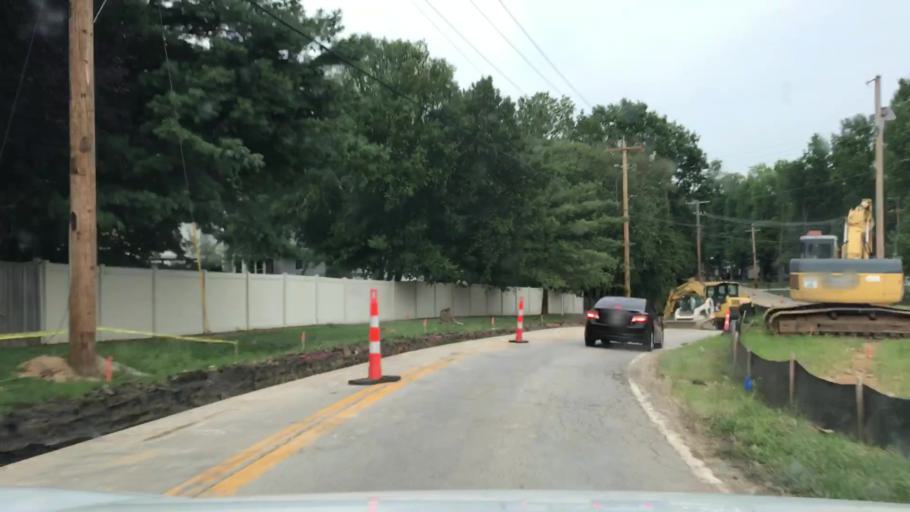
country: US
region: Missouri
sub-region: Saint Louis County
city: Ellisville
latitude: 38.5829
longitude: -90.5662
